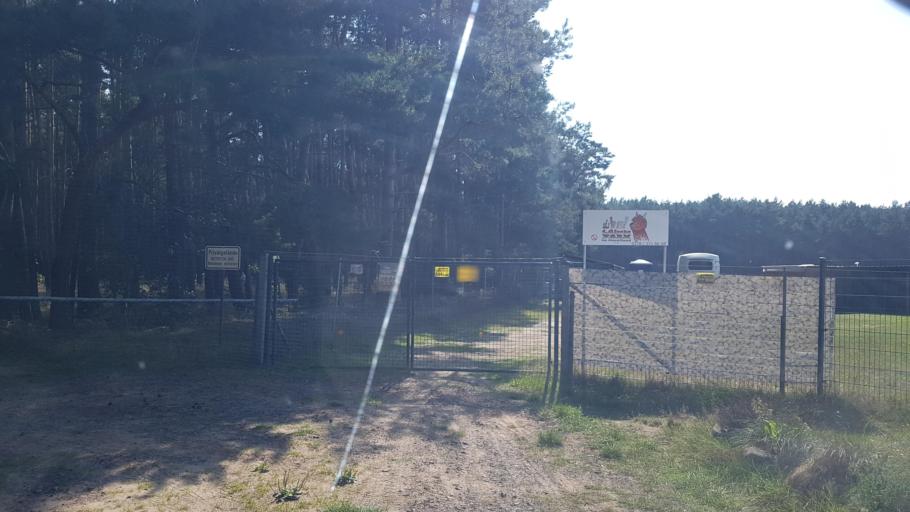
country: DE
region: Brandenburg
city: Nauen
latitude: 52.6792
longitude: 12.9392
